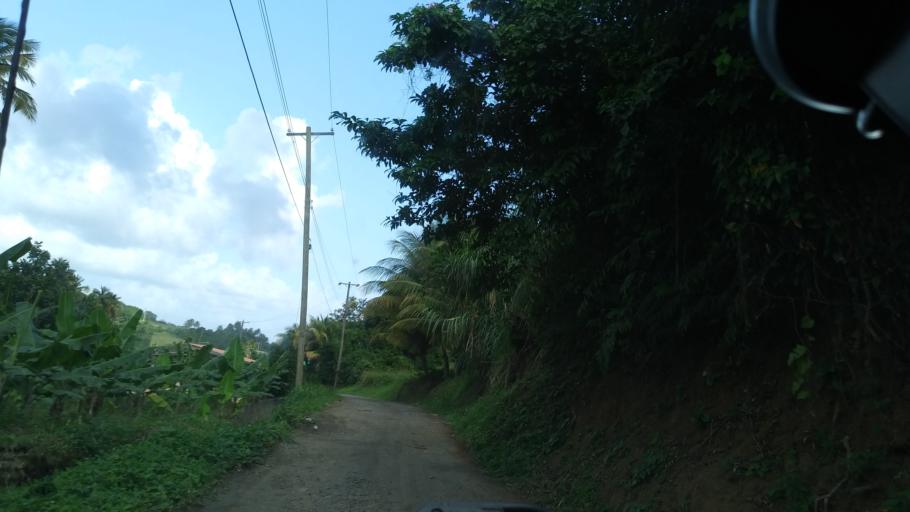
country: VC
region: Charlotte
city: Byera Village
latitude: 13.2317
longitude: -61.1306
